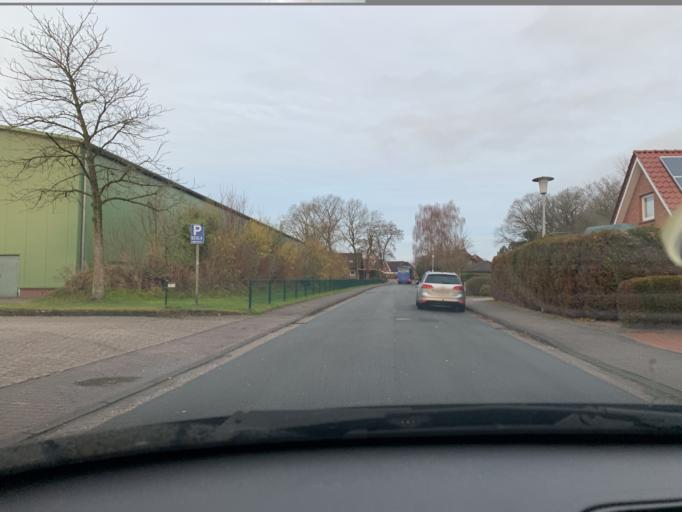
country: DE
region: Lower Saxony
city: Westerstede
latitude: 53.2531
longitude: 7.9111
